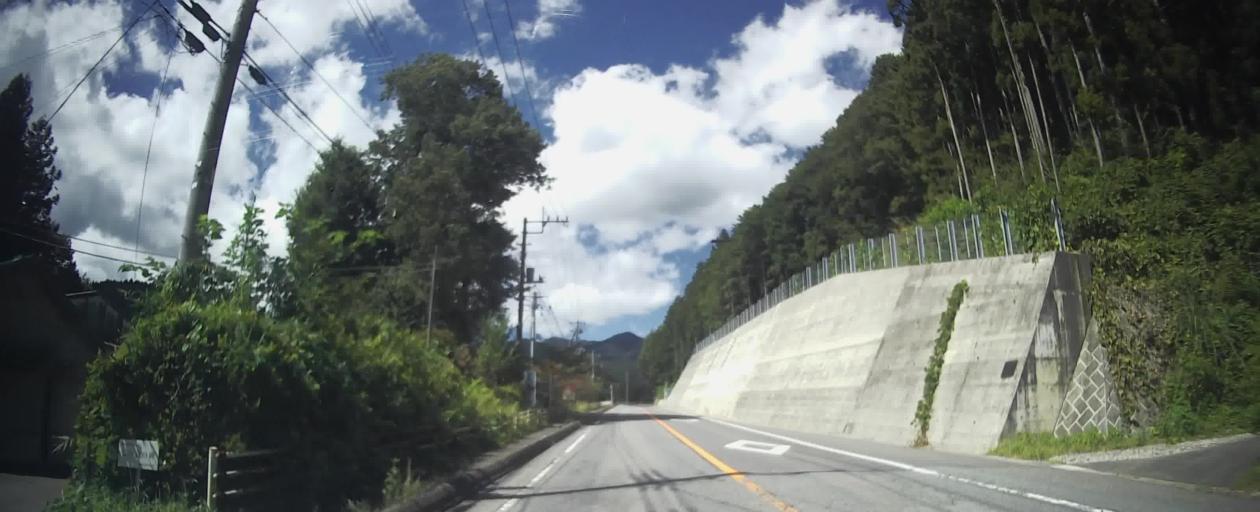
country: JP
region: Gunma
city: Kanekomachi
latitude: 36.4325
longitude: 138.9220
